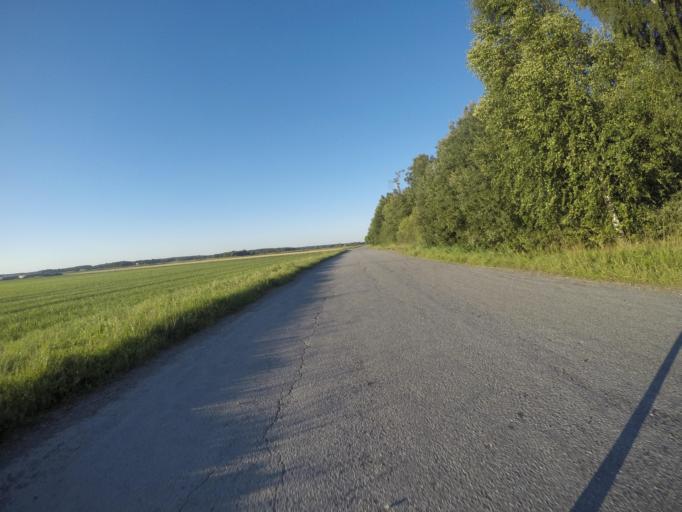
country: SE
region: Vaestmanland
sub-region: Vasteras
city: Vasteras
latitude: 59.5768
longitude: 16.6552
